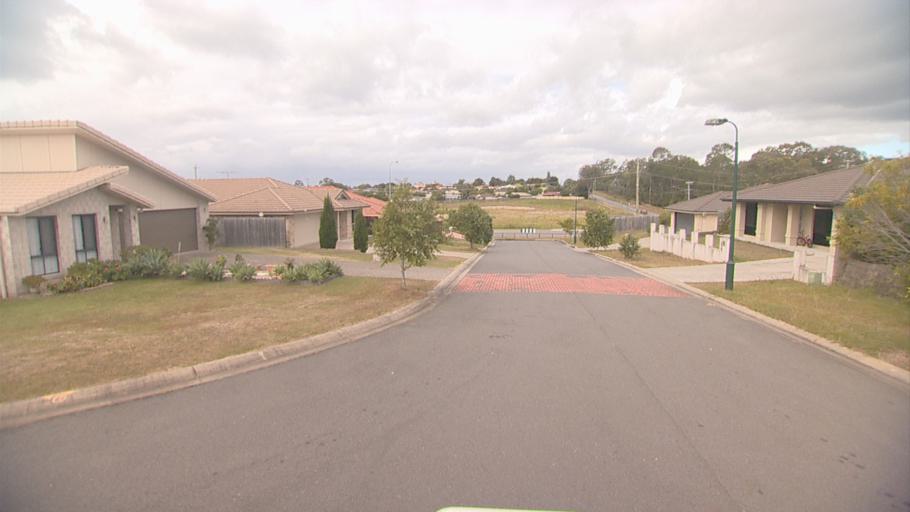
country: AU
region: Queensland
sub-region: Logan
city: Park Ridge South
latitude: -27.6886
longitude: 153.0483
